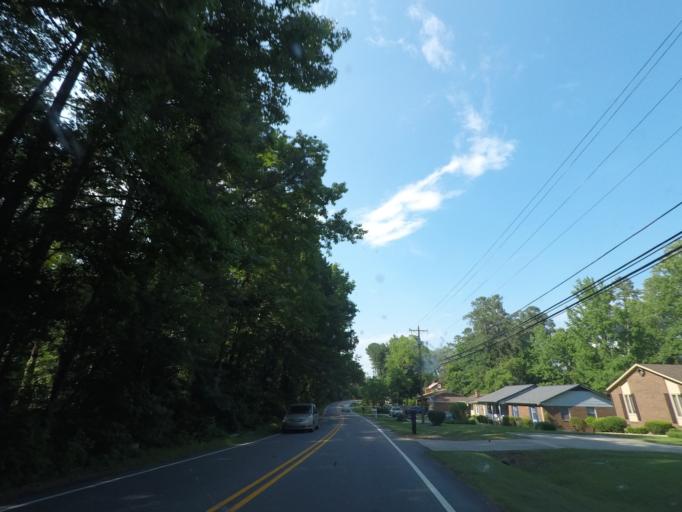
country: US
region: North Carolina
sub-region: Durham County
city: Durham
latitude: 35.9543
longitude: -78.9358
